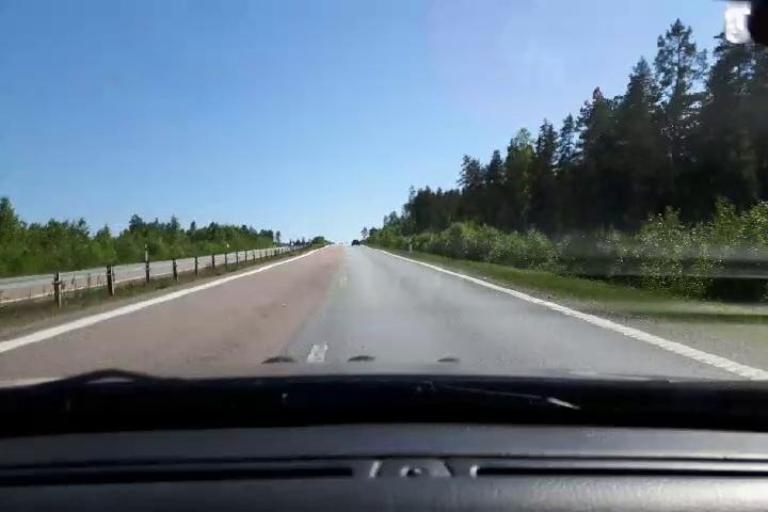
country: SE
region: Gaevleborg
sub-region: Soderhamns Kommun
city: Soderhamn
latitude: 61.3971
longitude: 16.9918
